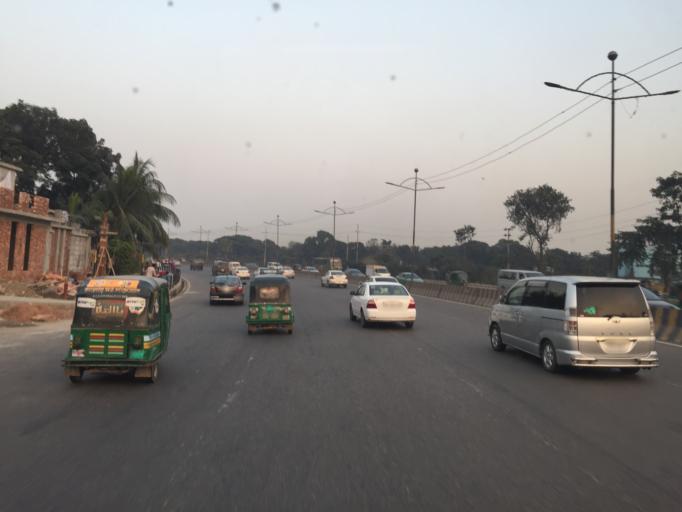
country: BD
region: Dhaka
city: Tungi
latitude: 23.8169
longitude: 90.4108
